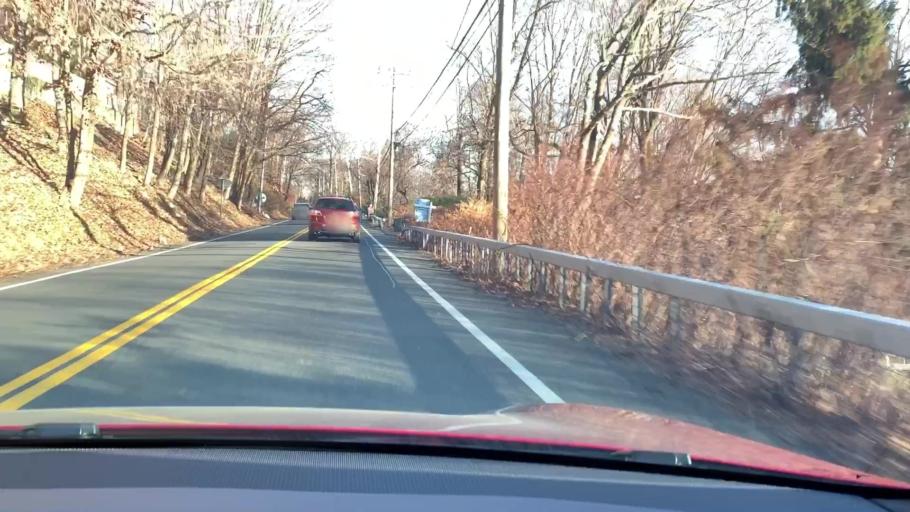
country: US
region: New York
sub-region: Rockland County
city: Piermont
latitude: 41.0571
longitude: -73.9231
